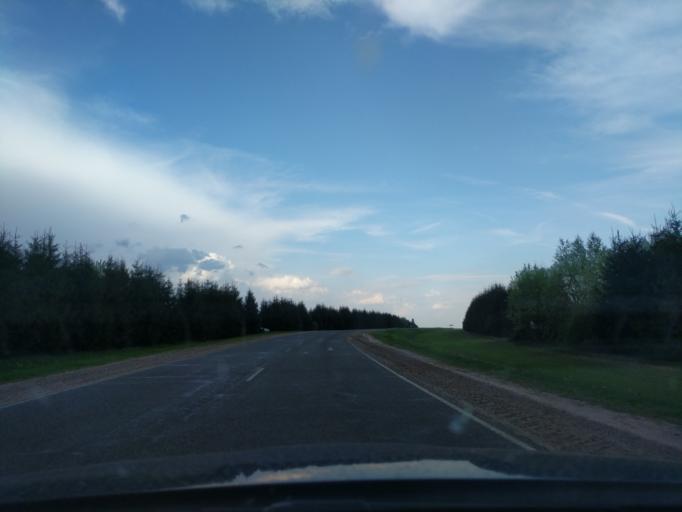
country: BY
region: Grodnenskaya
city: Navahrudak
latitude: 53.6387
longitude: 25.9120
